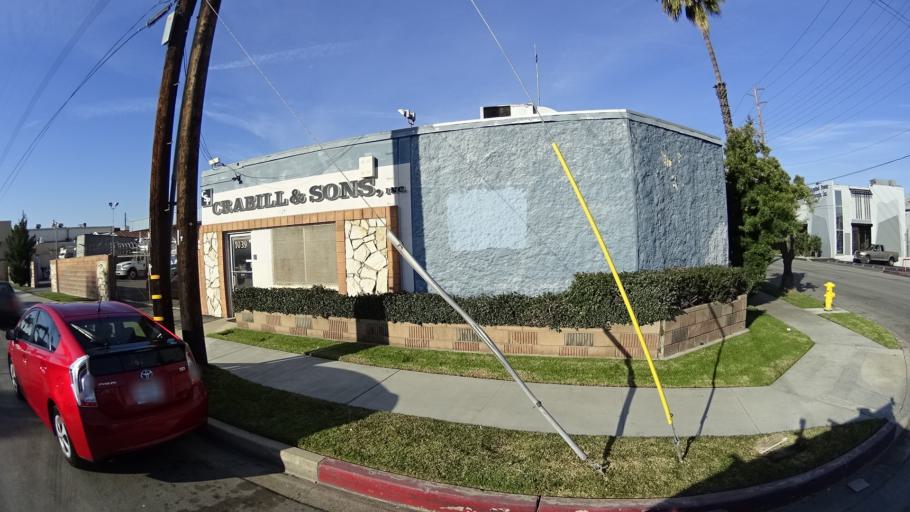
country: US
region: California
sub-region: Orange County
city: Anaheim
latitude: 33.8489
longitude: -117.9126
